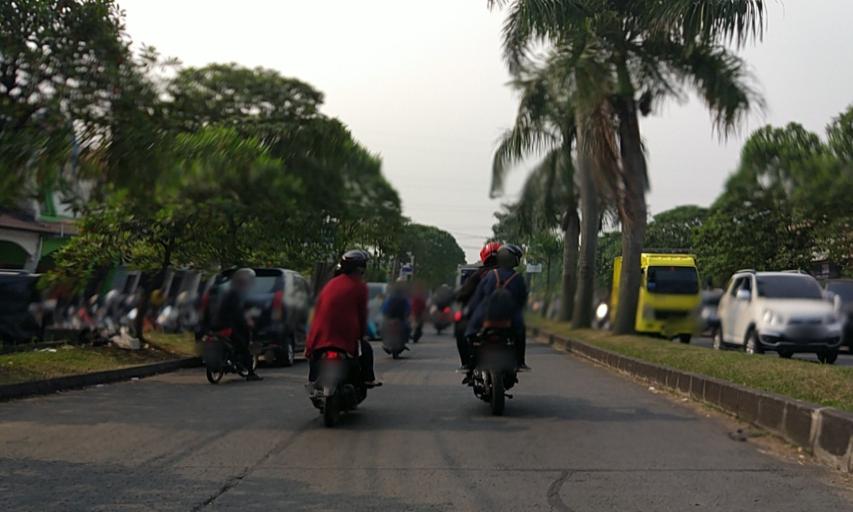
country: ID
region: West Java
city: Margahayukencana
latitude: -6.9552
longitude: 107.5620
